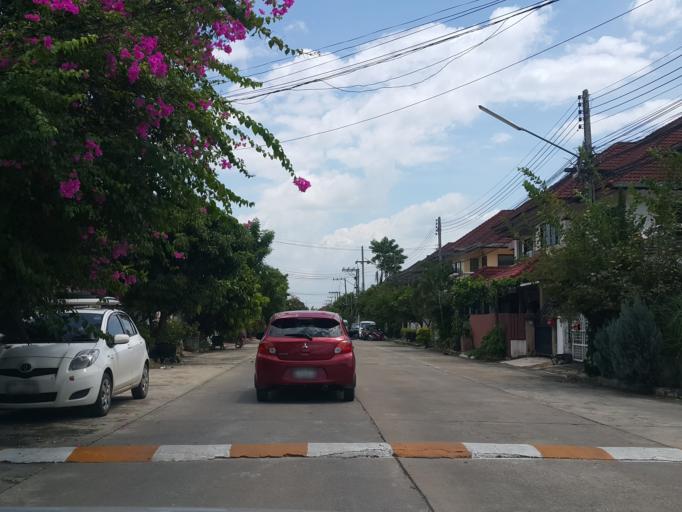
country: TH
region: Chiang Mai
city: Hang Dong
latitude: 18.7399
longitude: 98.9437
